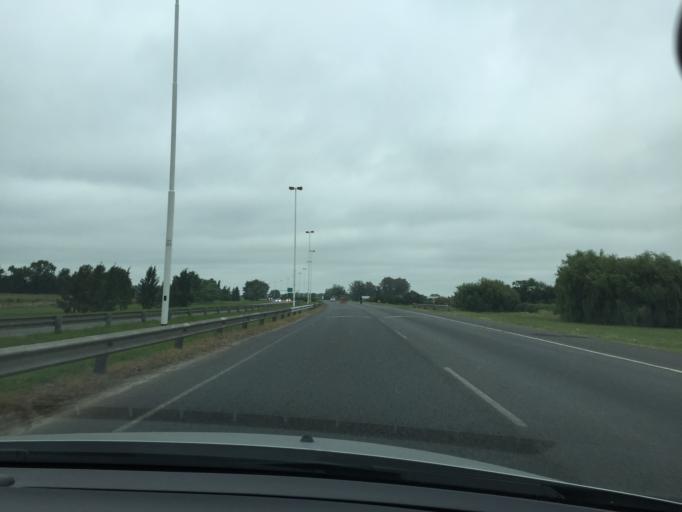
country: AR
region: Buenos Aires
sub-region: Partido de Ezeiza
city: Ezeiza
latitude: -34.8638
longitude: -58.5710
